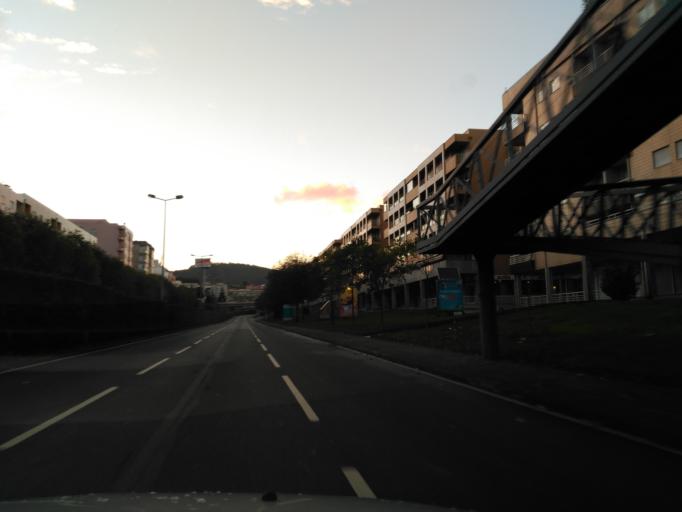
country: PT
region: Braga
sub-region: Braga
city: Braga
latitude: 41.5450
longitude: -8.4046
